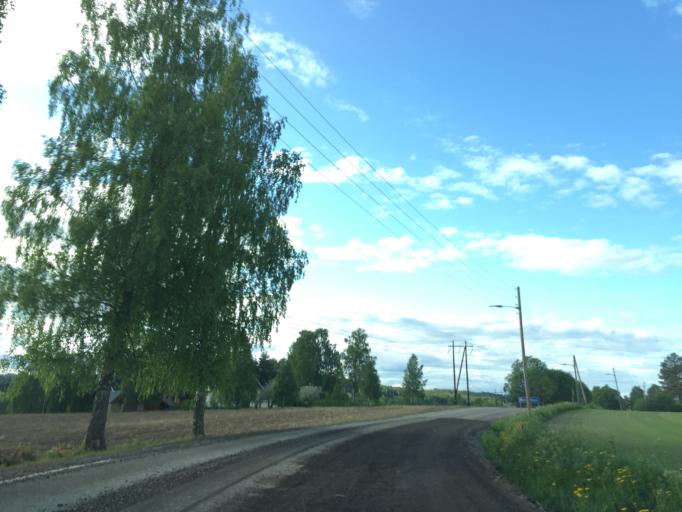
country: NO
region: Akershus
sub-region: Nes
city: Auli
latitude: 60.0209
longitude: 11.3276
